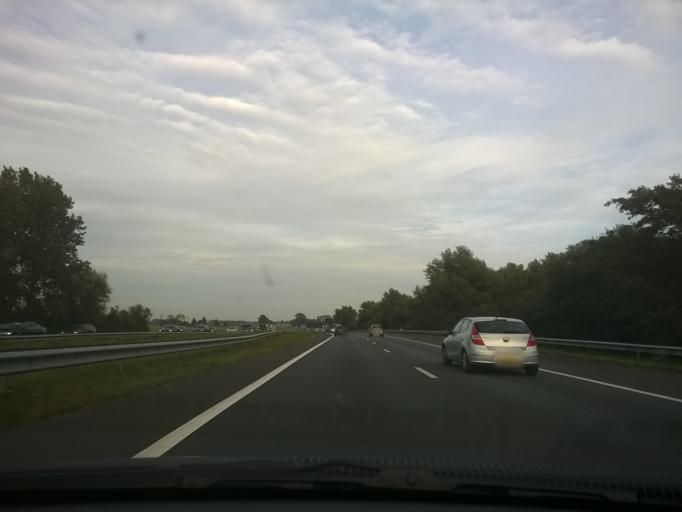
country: NL
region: Groningen
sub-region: Gemeente Zuidhorn
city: Aduard
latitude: 53.1971
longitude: 6.4493
